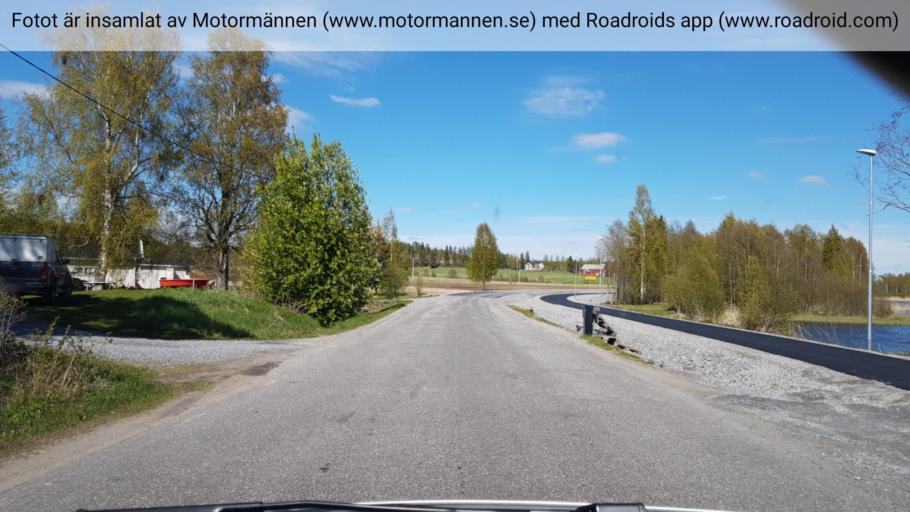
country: SE
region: Vaesterbotten
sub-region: Vannas Kommun
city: Vannasby
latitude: 64.0279
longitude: 20.0270
